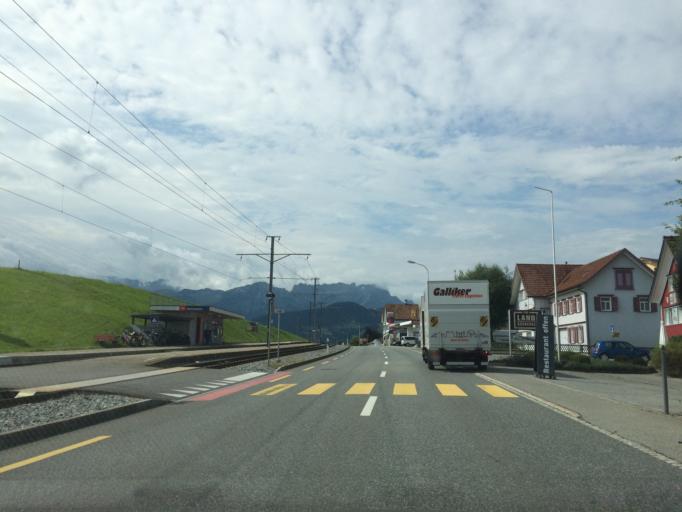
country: CH
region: Appenzell Ausserrhoden
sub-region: Bezirk Mittelland
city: Gais
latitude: 47.3488
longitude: 9.4327
